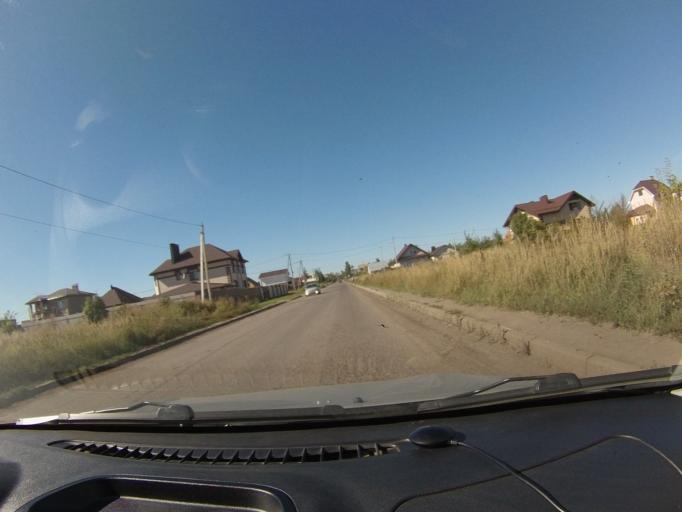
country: RU
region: Tambov
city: Tambov
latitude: 52.7641
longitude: 41.3701
